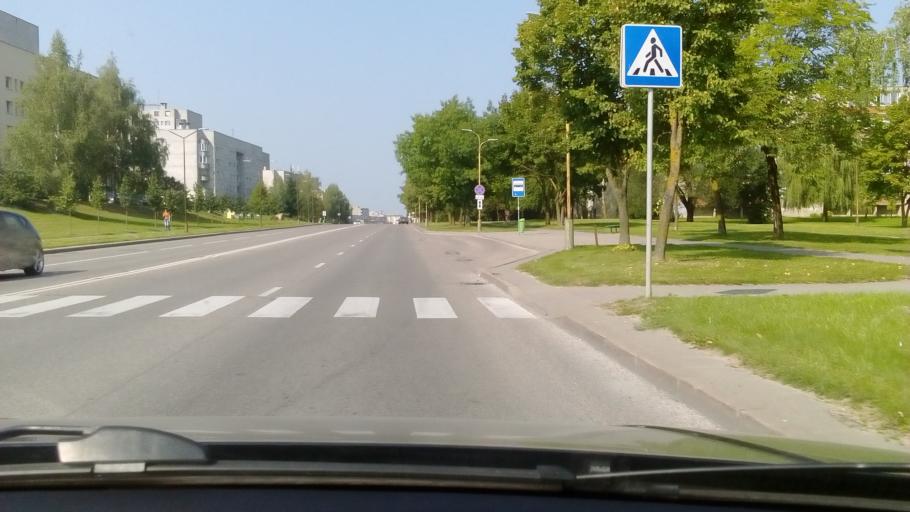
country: LT
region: Alytaus apskritis
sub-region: Alytus
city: Alytus
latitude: 54.3890
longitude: 24.0243
